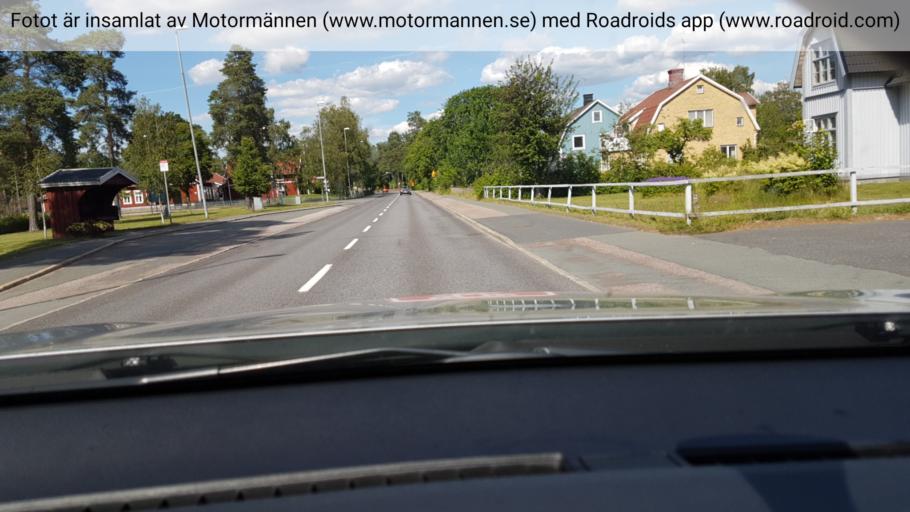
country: SE
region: Joenkoeping
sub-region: Vaggeryds Kommun
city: Vaggeryd
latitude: 57.4908
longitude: 14.1279
